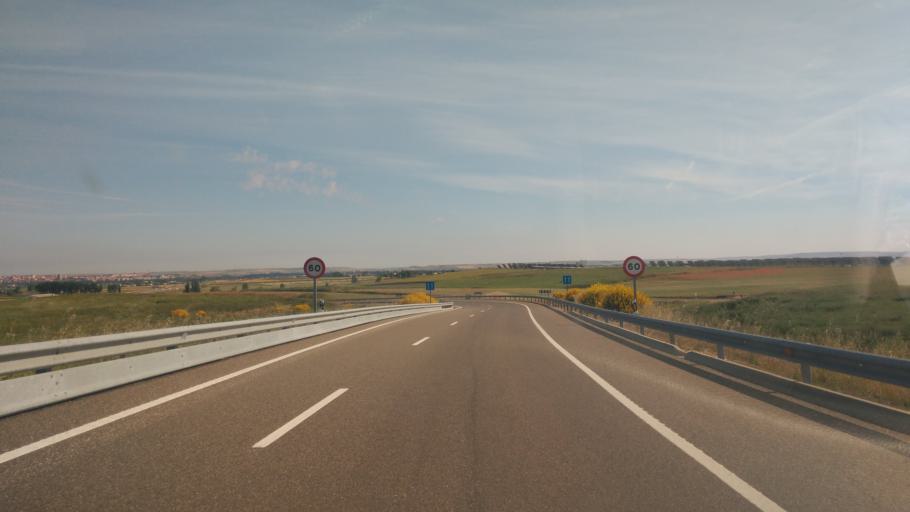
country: ES
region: Castille and Leon
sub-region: Provincia de Zamora
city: Morales del Vino
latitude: 41.4525
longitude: -5.7205
